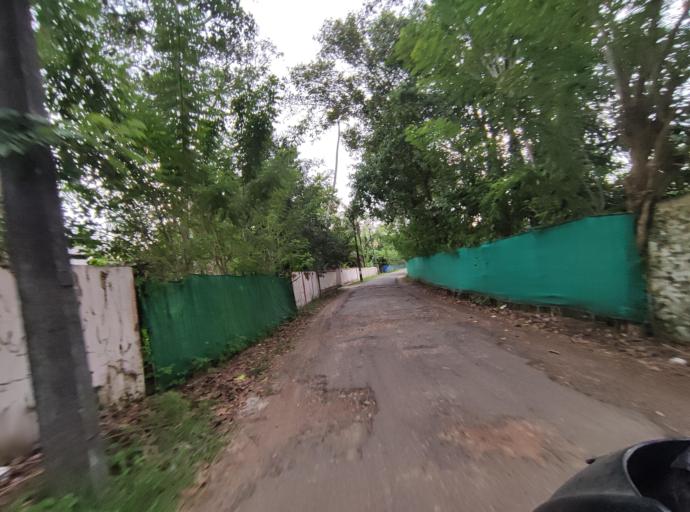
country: IN
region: Kerala
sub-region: Alappuzha
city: Shertallai
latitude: 9.6704
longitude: 76.3444
